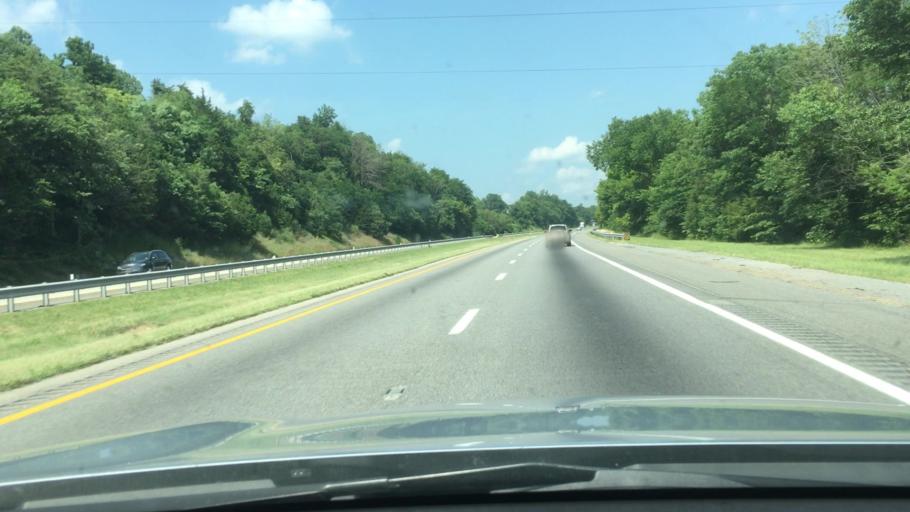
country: US
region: Virginia
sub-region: Botetourt County
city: Buchanan
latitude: 37.5880
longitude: -79.6368
